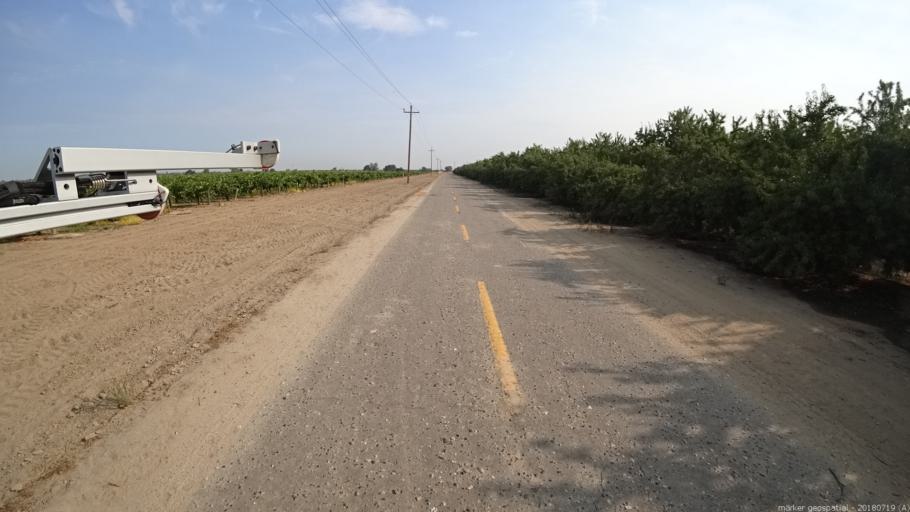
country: US
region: California
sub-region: Madera County
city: Fairmead
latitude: 37.1097
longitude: -120.2113
